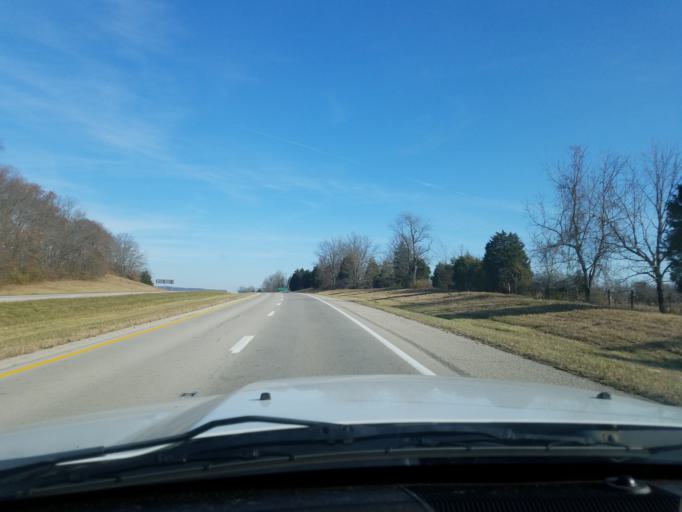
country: US
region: Ohio
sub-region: Adams County
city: Peebles
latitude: 38.9388
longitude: -83.3874
